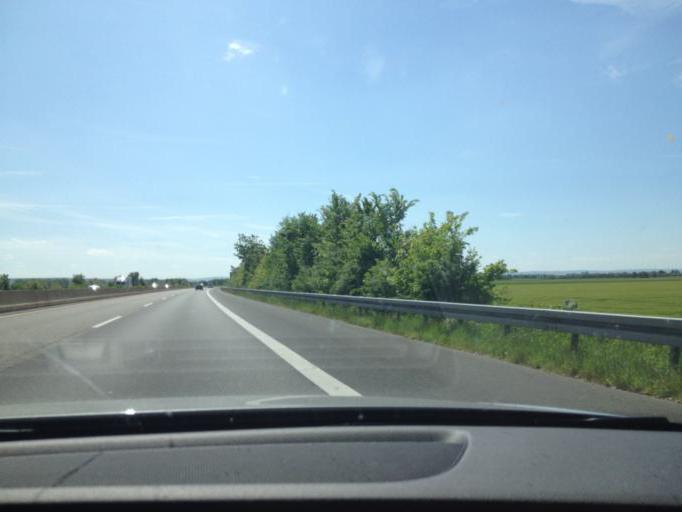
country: DE
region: North Rhine-Westphalia
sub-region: Regierungsbezirk Koln
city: Euskirchen
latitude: 50.6938
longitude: 6.7659
